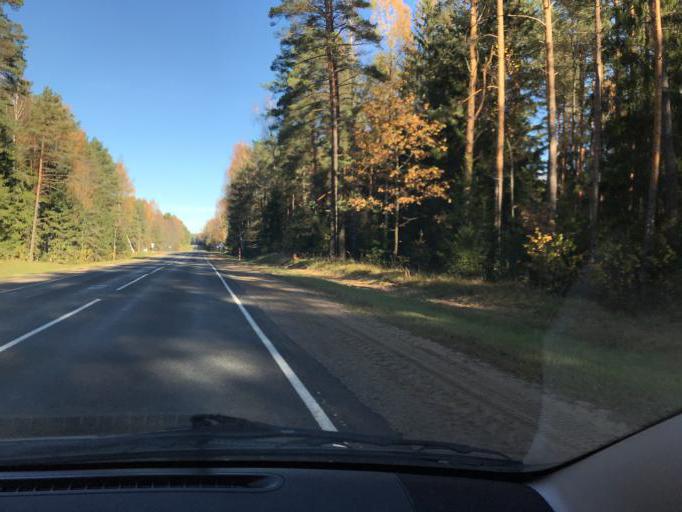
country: BY
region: Vitebsk
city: Polatsk
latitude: 55.3730
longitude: 28.8105
